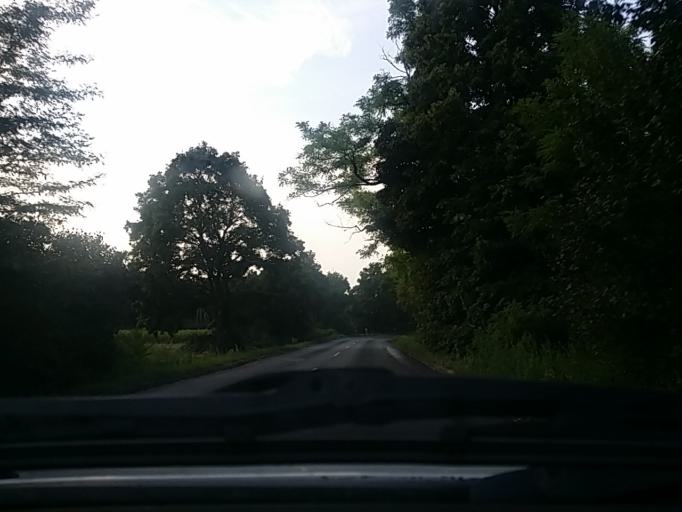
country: HU
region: Fejer
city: Csakvar
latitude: 47.4331
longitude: 18.5319
